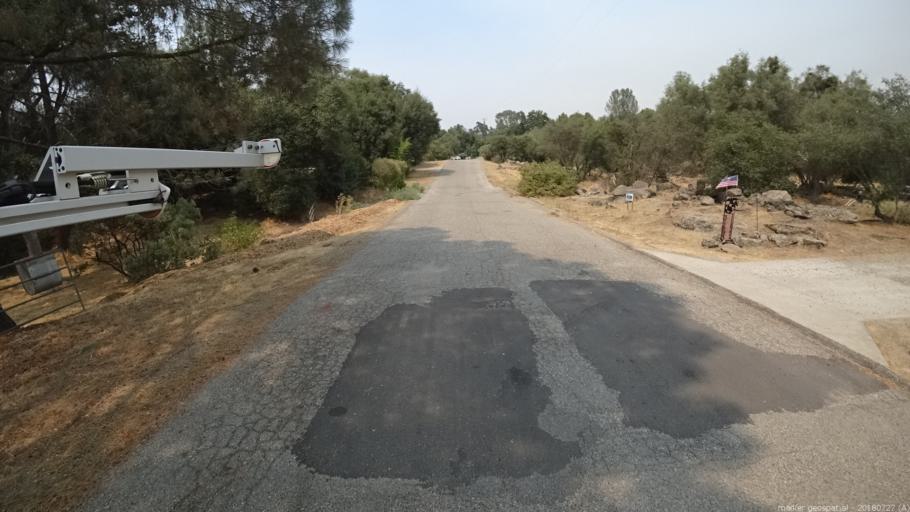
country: US
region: California
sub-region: Madera County
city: Coarsegold
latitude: 37.2079
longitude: -119.6753
